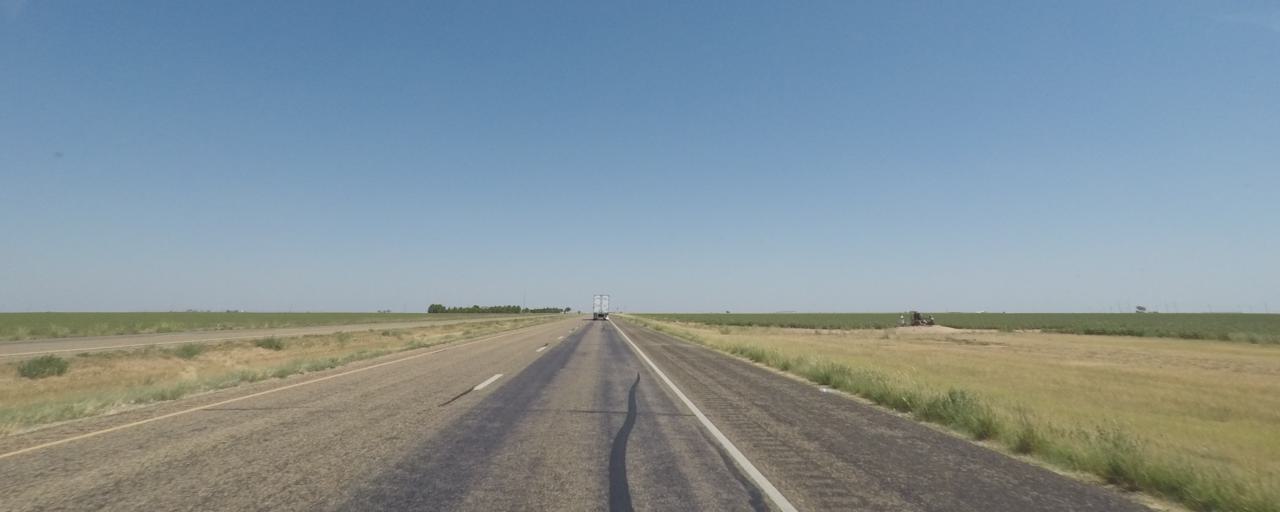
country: US
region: Texas
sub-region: Crosby County
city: Ralls
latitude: 33.6704
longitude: -101.3510
